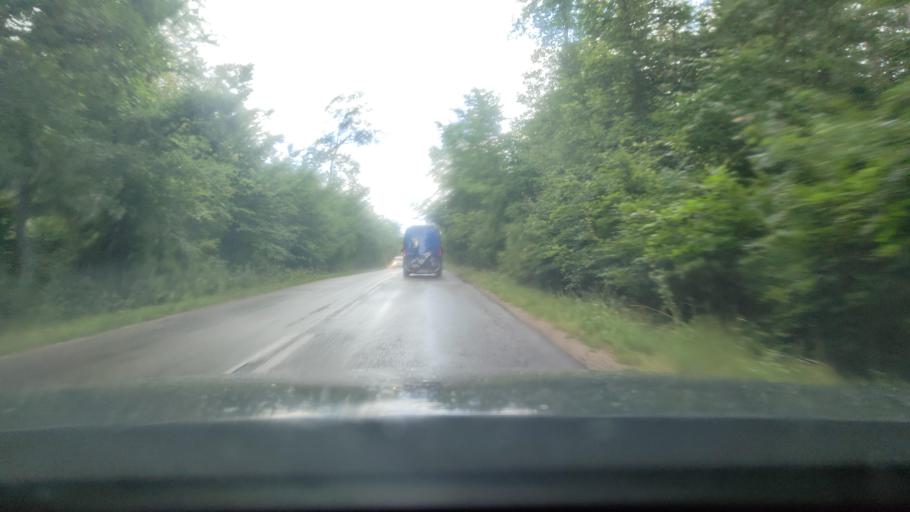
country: PL
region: Pomeranian Voivodeship
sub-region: Powiat wejherowski
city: Orle
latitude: 54.7027
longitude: 18.1736
